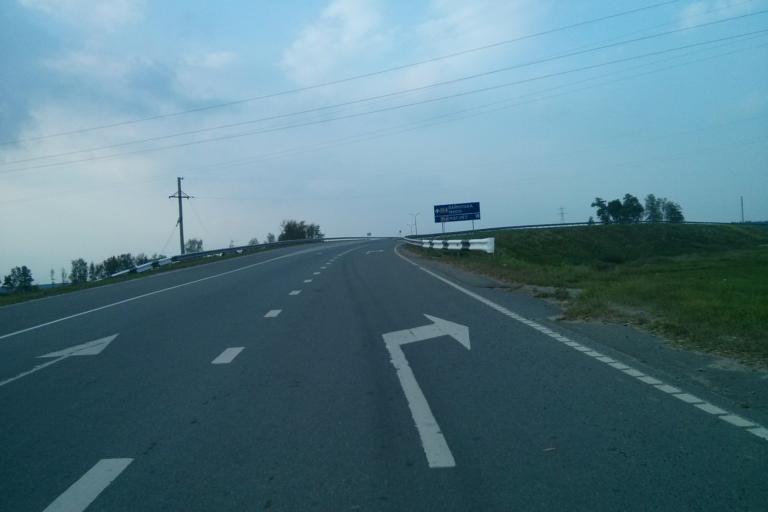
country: BY
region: Minsk
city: Chervyen'
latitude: 53.7211
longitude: 28.3959
